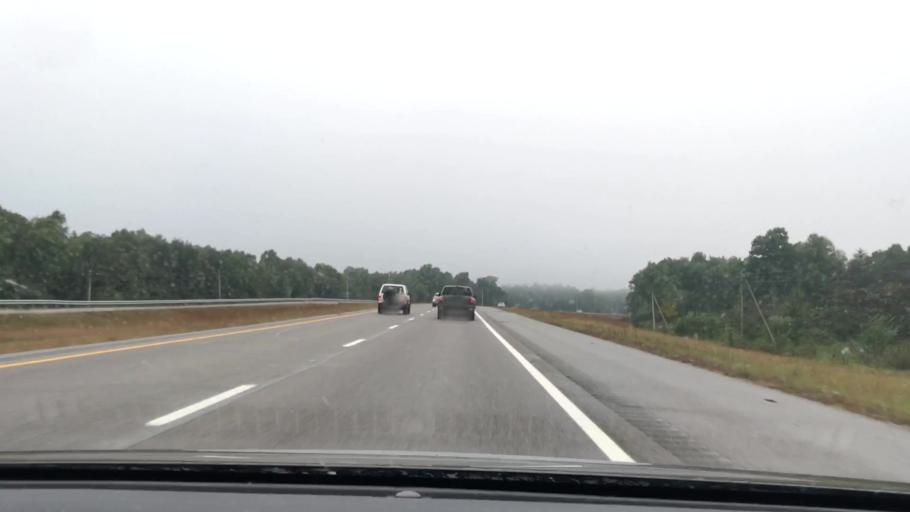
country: US
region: Tennessee
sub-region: Fentress County
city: Jamestown
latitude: 36.3472
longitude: -84.9523
